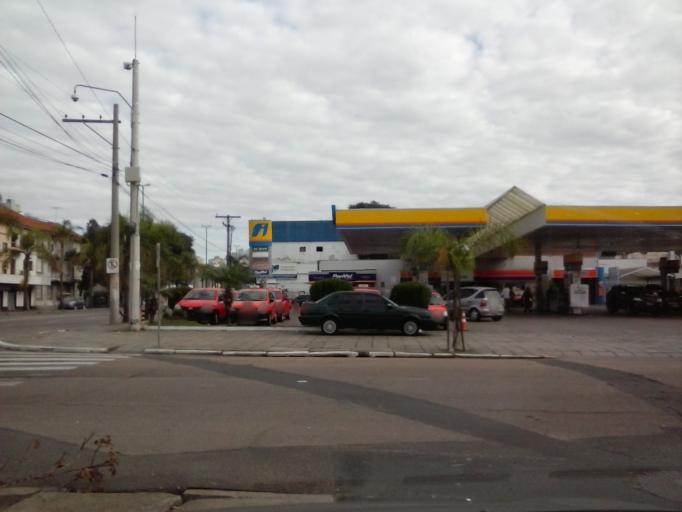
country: BR
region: Rio Grande do Sul
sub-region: Porto Alegre
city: Porto Alegre
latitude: -30.0221
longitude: -51.2124
